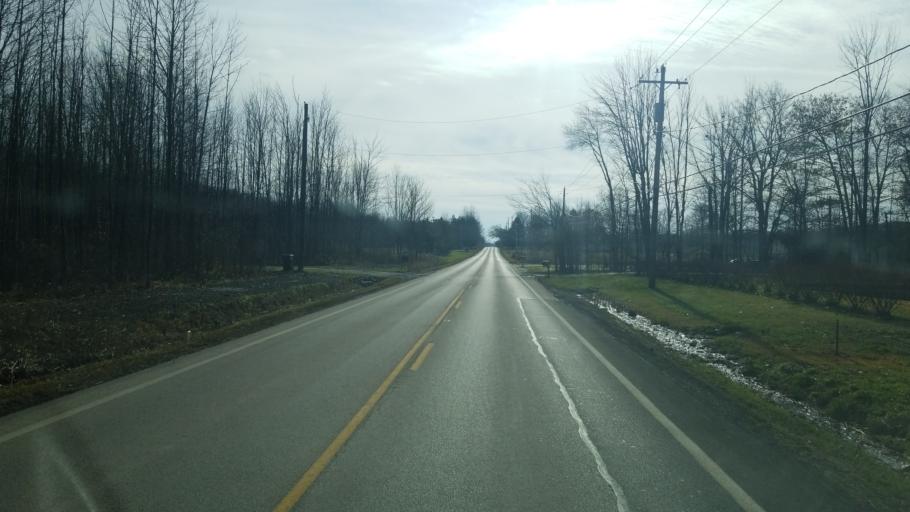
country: US
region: Ohio
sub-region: Ashtabula County
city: Geneva
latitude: 41.7278
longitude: -80.9524
